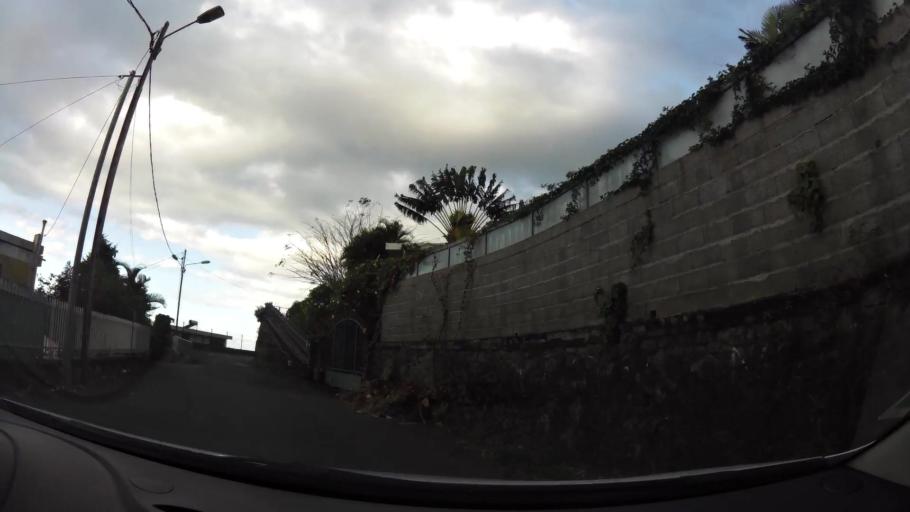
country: RE
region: Reunion
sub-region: Reunion
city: Saint-Denis
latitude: -20.9010
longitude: 55.4449
